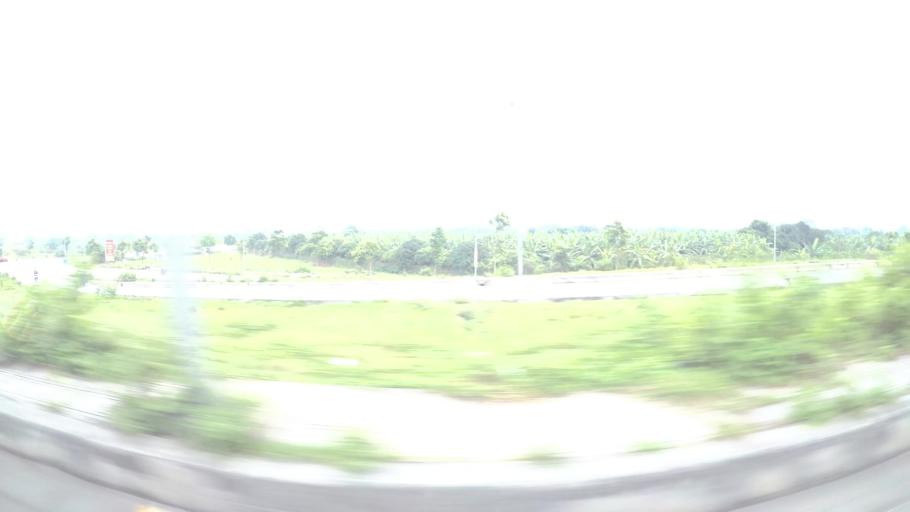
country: VN
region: Ha Noi
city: Hoan Kiem
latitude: 21.0765
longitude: 105.8958
